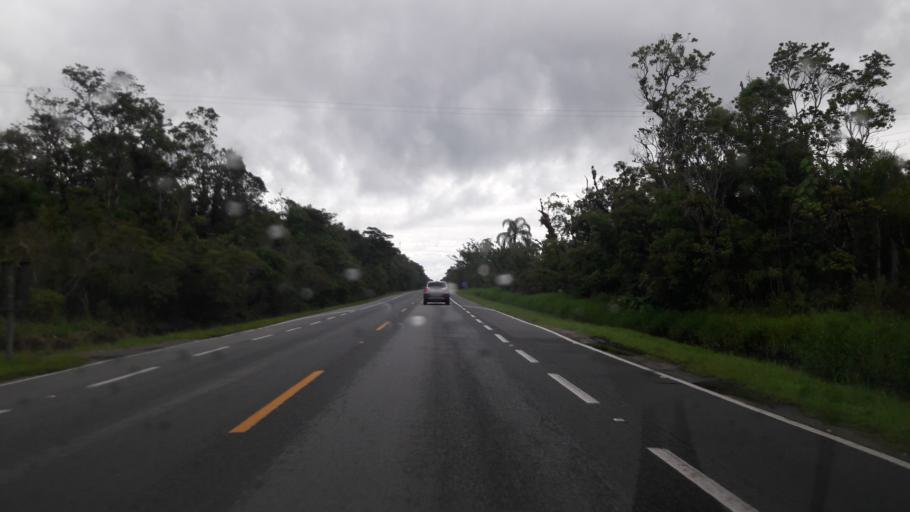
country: BR
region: Parana
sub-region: Pontal Do Parana
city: Pontal do Parana
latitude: -25.6485
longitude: -48.5278
